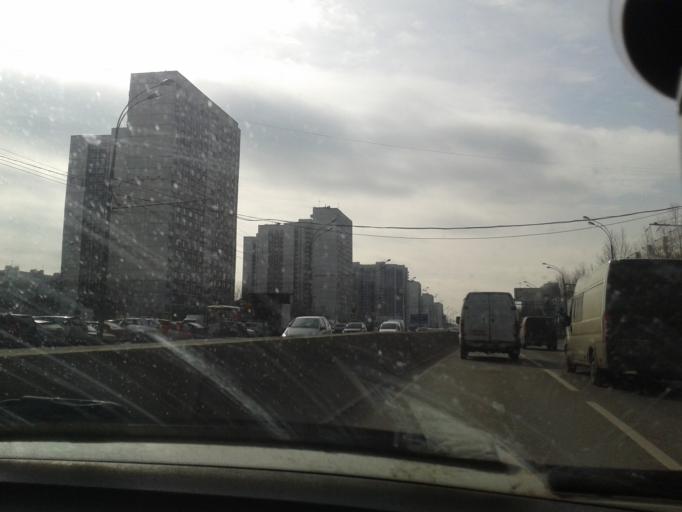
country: RU
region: Moscow
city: Lianozovo
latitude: 55.9029
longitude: 37.5870
